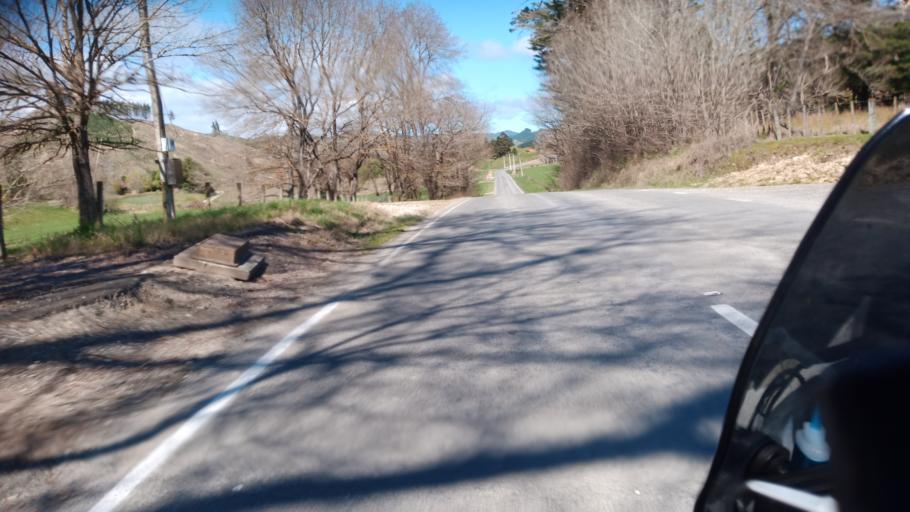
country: NZ
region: Gisborne
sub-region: Gisborne District
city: Gisborne
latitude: -38.7325
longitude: 177.8258
